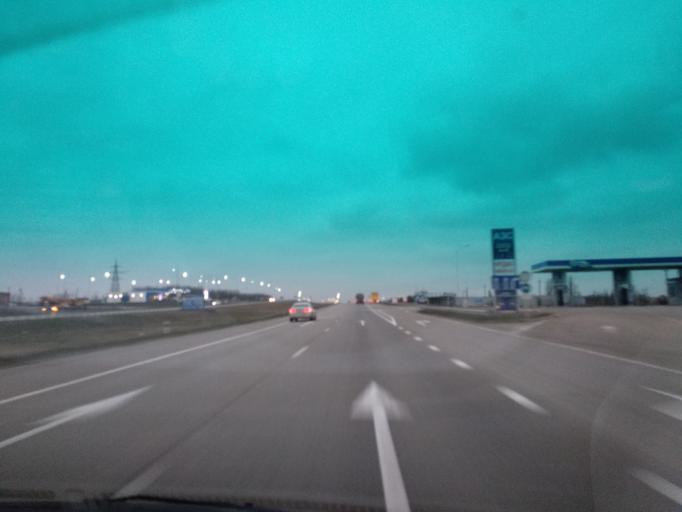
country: RU
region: Adygeya
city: Adygeysk
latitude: 44.9063
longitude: 39.1559
